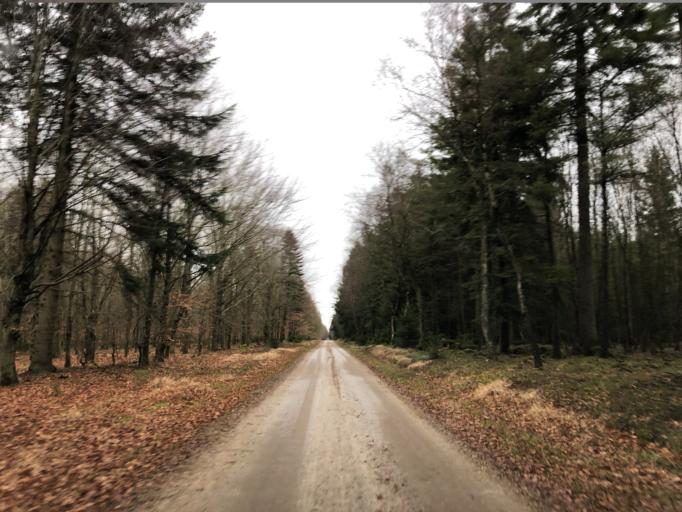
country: DK
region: Central Jutland
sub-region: Holstebro Kommune
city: Vinderup
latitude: 56.3849
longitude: 8.8669
